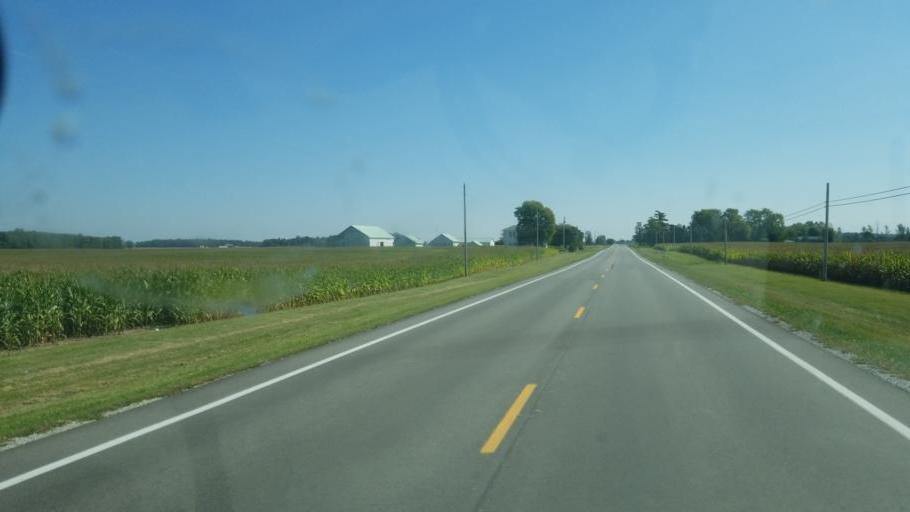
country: US
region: Ohio
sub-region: Hardin County
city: Kenton
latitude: 40.6429
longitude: -83.4960
